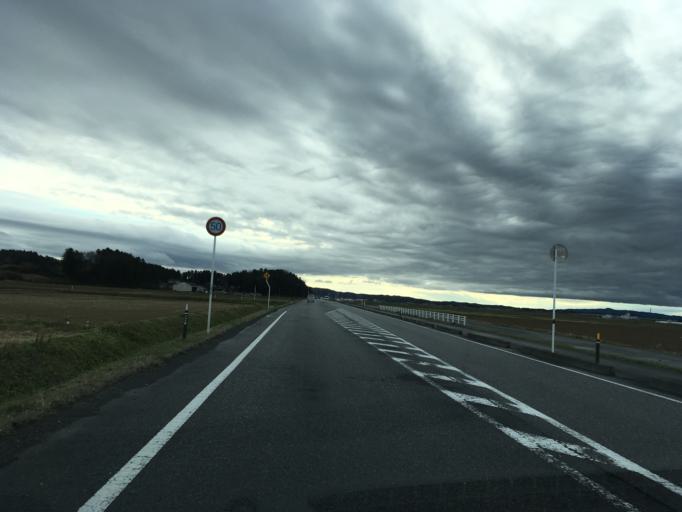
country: JP
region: Miyagi
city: Wakuya
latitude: 38.7008
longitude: 141.2602
